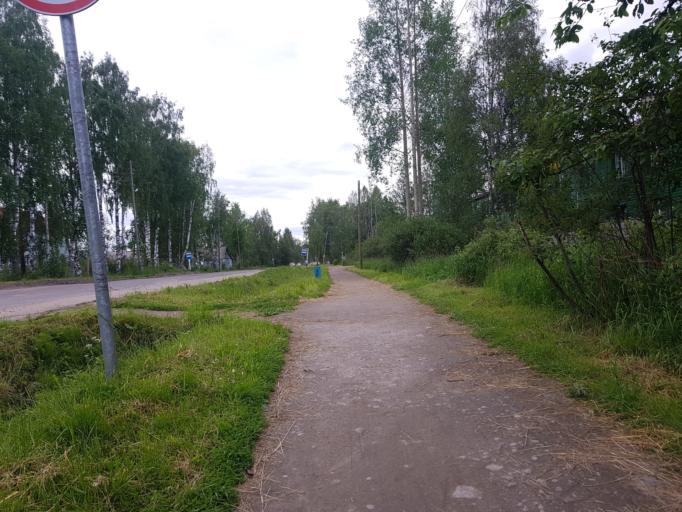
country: RU
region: Republic of Karelia
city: Kalevala
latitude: 65.2019
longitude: 31.1759
